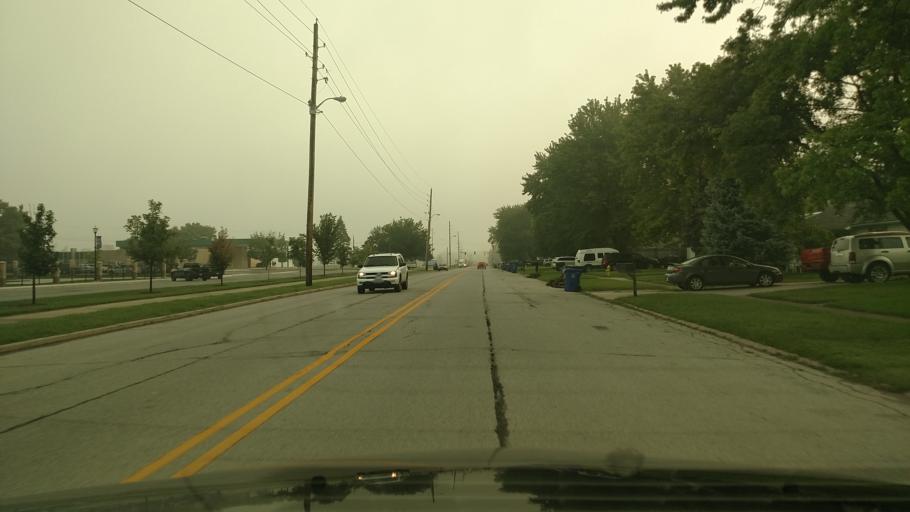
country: US
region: Indiana
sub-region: Howard County
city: Kokomo
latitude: 40.4588
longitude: -86.1555
